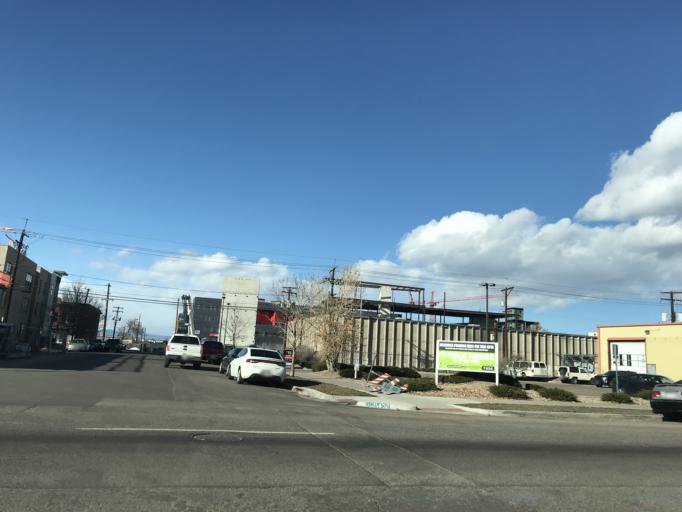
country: US
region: Colorado
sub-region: Denver County
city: Denver
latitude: 39.7676
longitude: -104.9753
